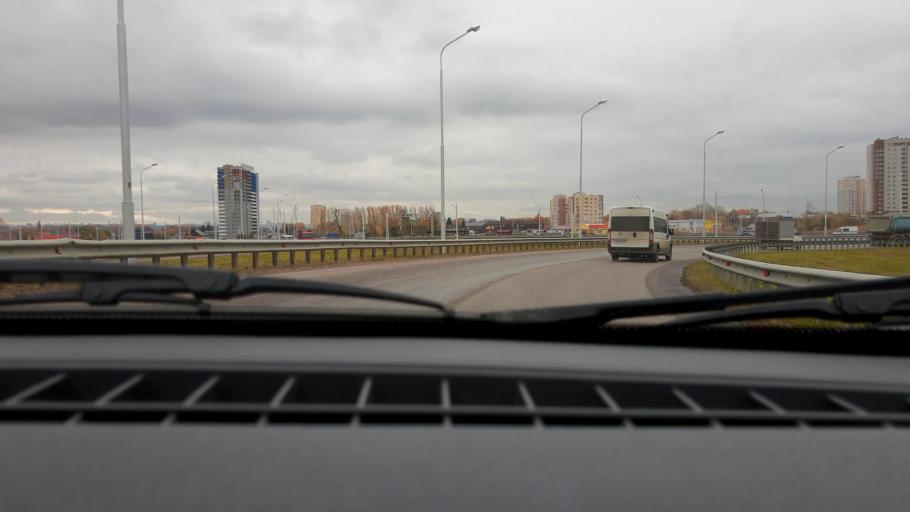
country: RU
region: Bashkortostan
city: Mikhaylovka
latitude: 54.7995
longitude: 55.8708
